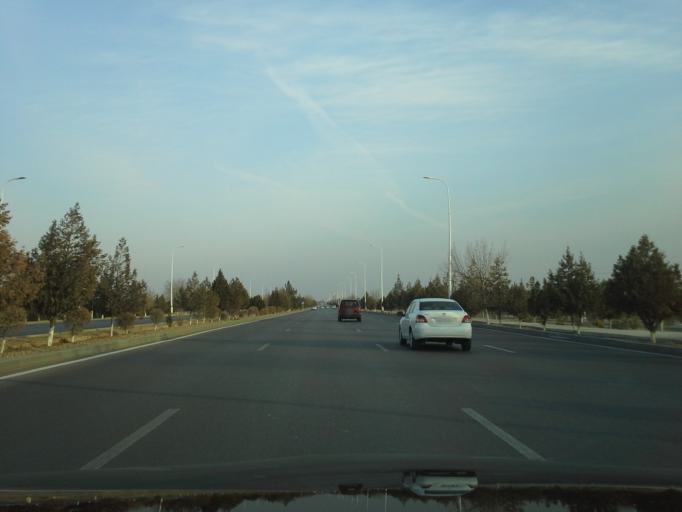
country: TM
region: Ahal
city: Abadan
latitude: 38.0412
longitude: 58.2096
